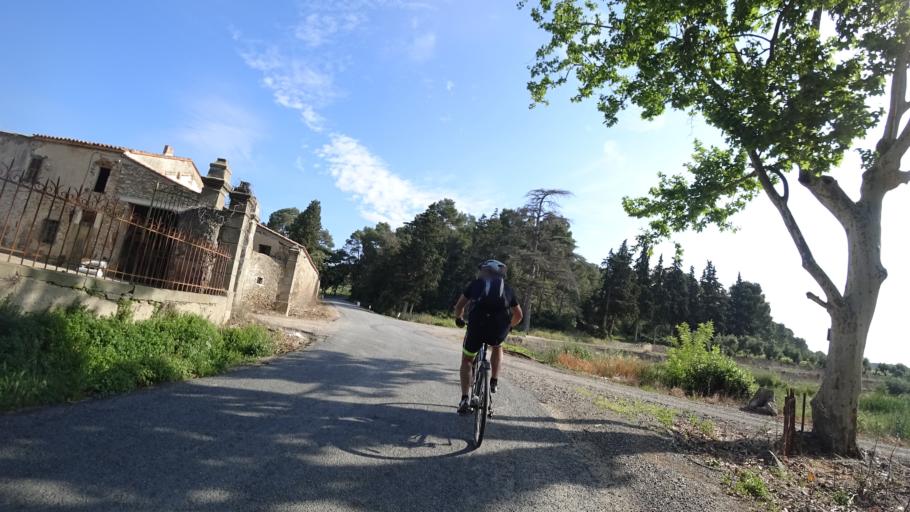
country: FR
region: Languedoc-Roussillon
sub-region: Departement de l'Herault
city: Olonzac
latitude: 43.2433
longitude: 2.7192
